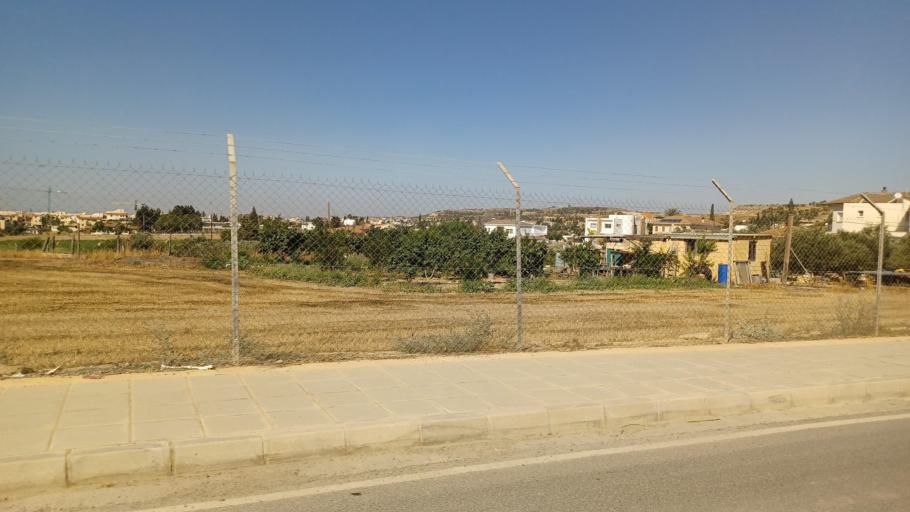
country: CY
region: Larnaka
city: Pyla
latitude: 35.0132
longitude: 33.6970
